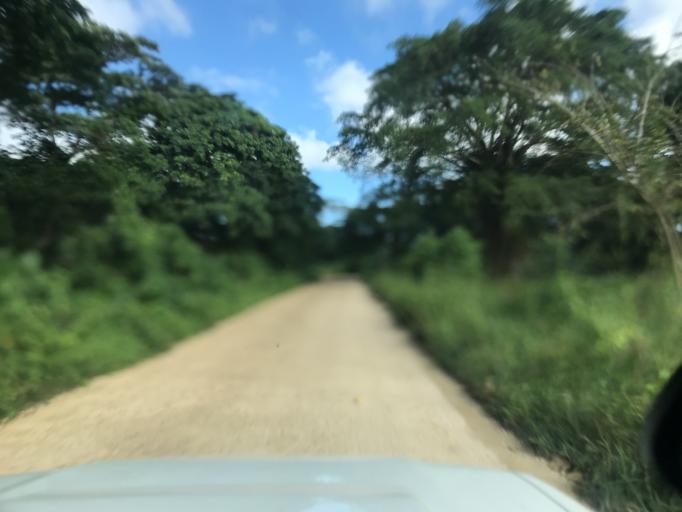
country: VU
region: Sanma
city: Luganville
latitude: -15.5100
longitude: 167.1215
